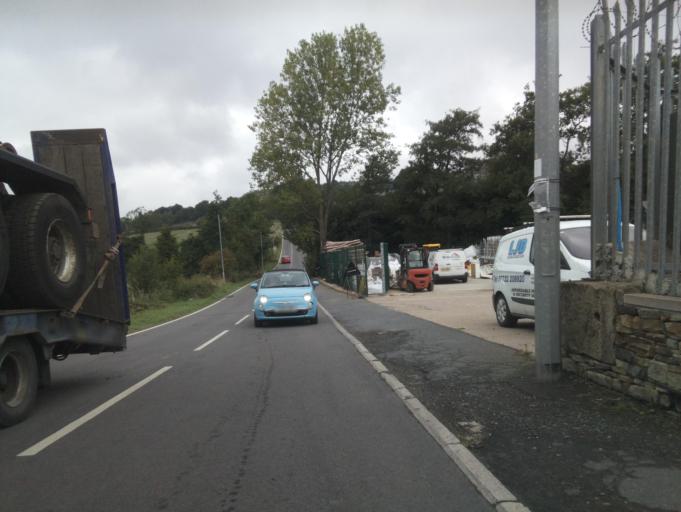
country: GB
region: England
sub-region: Kirklees
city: Shelley
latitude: 53.5923
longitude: -1.6885
